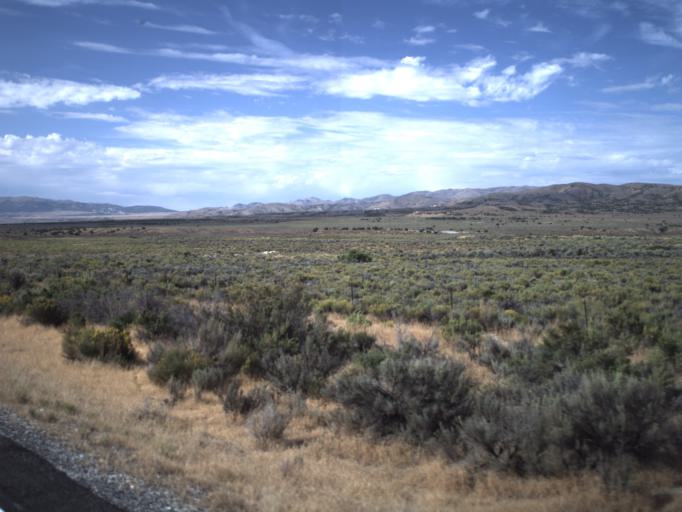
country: US
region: Idaho
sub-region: Cassia County
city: Burley
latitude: 41.6683
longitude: -113.5451
